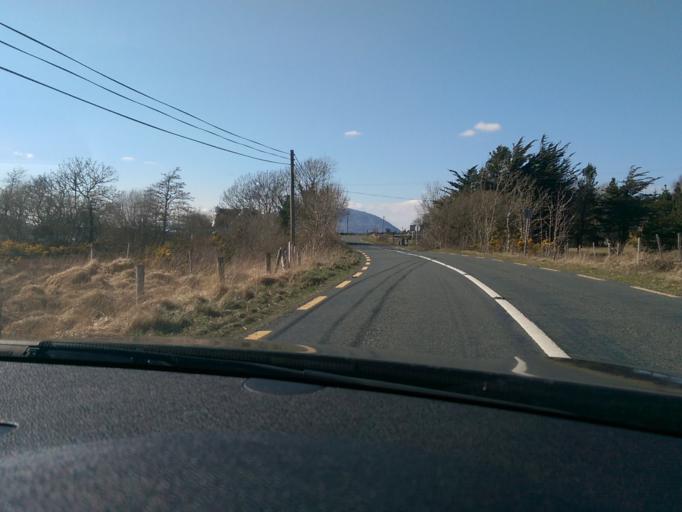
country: IE
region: Connaught
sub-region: County Galway
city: Oughterard
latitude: 53.4365
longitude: -9.4410
